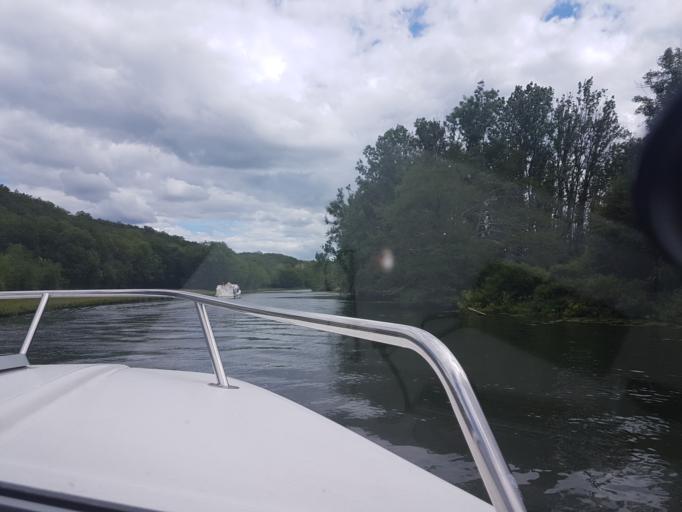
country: FR
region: Bourgogne
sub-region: Departement de l'Yonne
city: Vermenton
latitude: 47.5845
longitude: 3.6431
